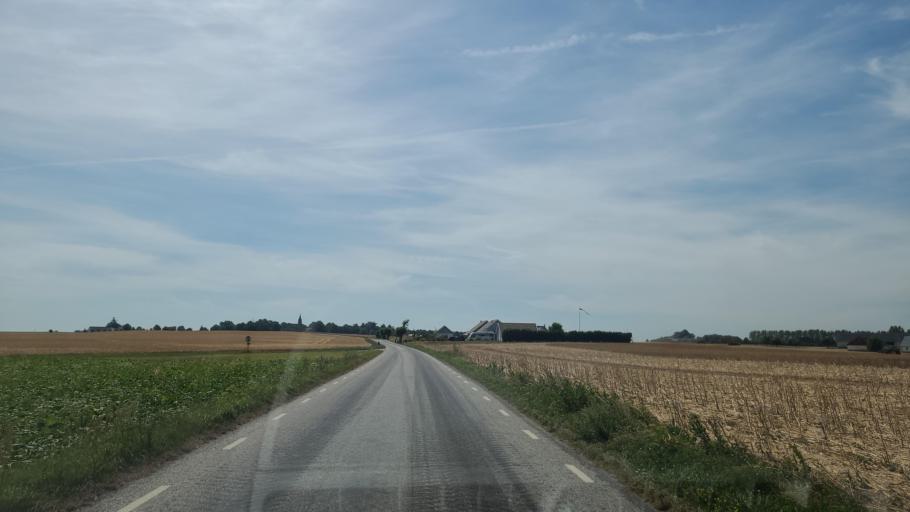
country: SE
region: Skane
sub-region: Vellinge Kommun
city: Vellinge
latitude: 55.4585
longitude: 13.0917
